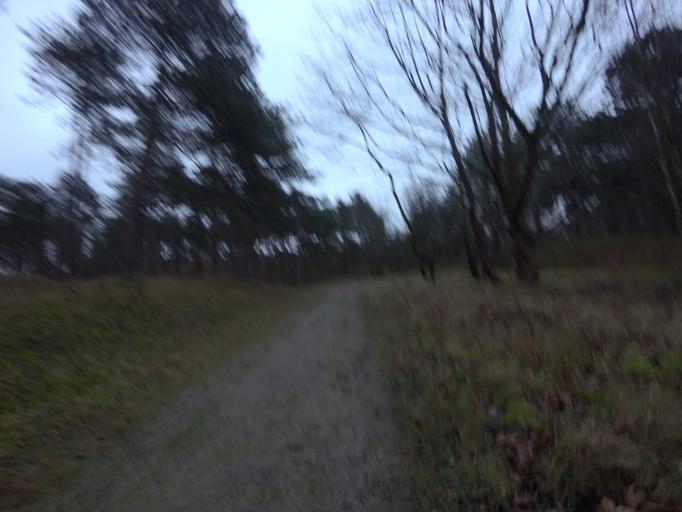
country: NL
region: Zeeland
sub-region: Schouwen-Duiveland
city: Burgh
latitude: 51.6792
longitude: 3.7009
